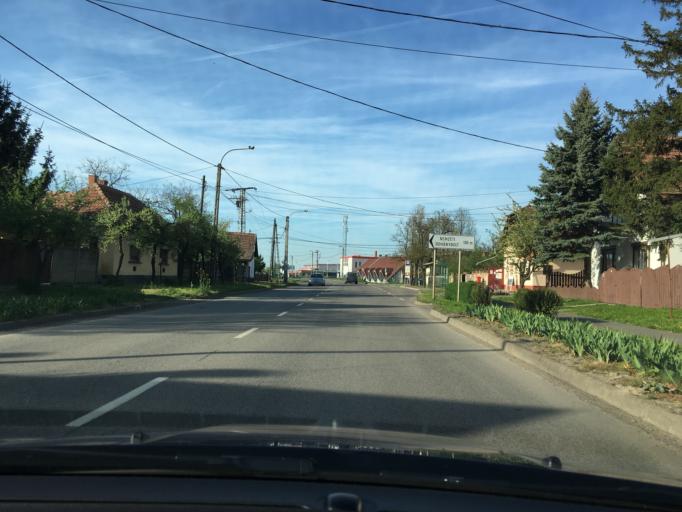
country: HU
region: Bekes
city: Korosladany
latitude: 46.9662
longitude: 21.0883
